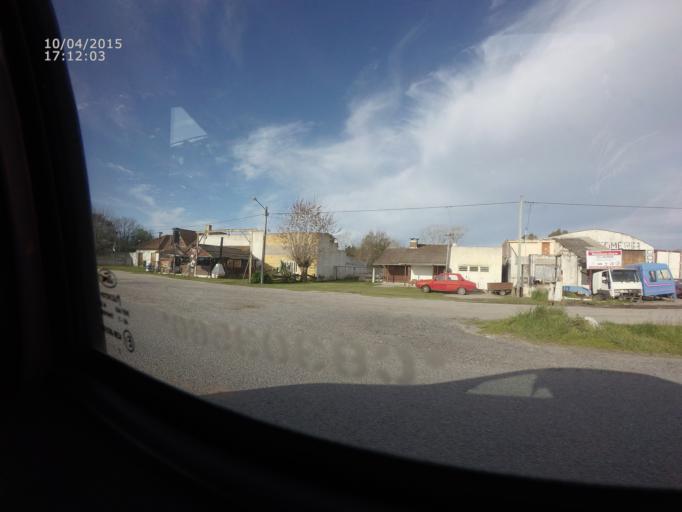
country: AR
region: Buenos Aires
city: Coronel Vidal
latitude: -37.2748
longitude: -57.7662
